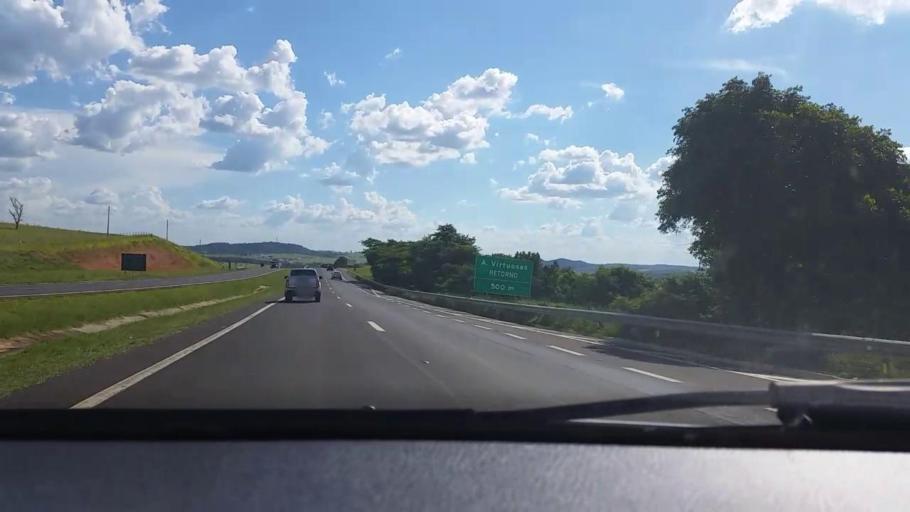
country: BR
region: Sao Paulo
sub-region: Bauru
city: Bauru
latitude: -22.3932
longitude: -49.0814
